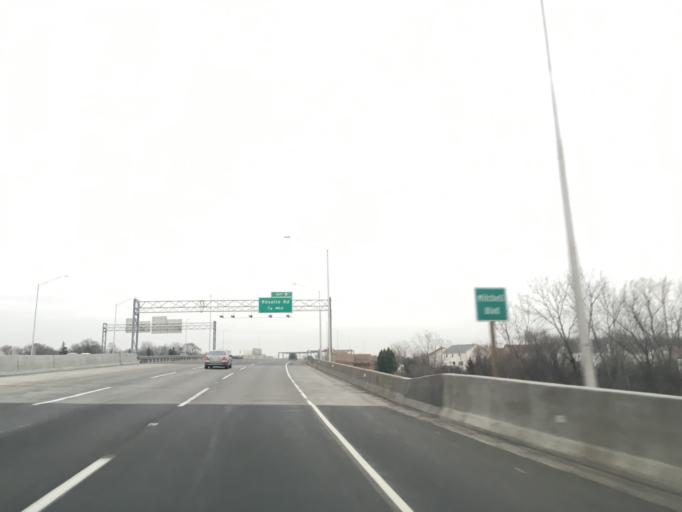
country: US
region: Illinois
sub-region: DuPage County
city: Roselle
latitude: 41.9975
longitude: -88.0924
